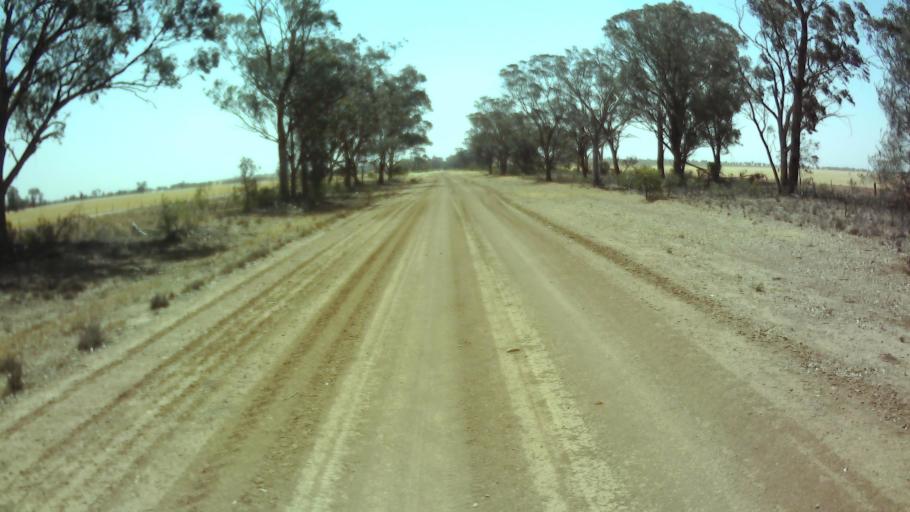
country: AU
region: New South Wales
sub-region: Weddin
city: Grenfell
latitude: -33.9195
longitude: 147.7778
